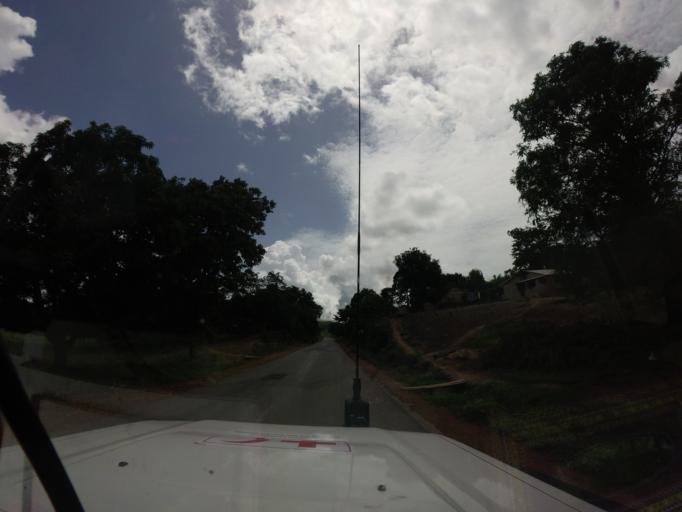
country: SL
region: Northern Province
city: Bindi
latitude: 10.1722
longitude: -11.2958
